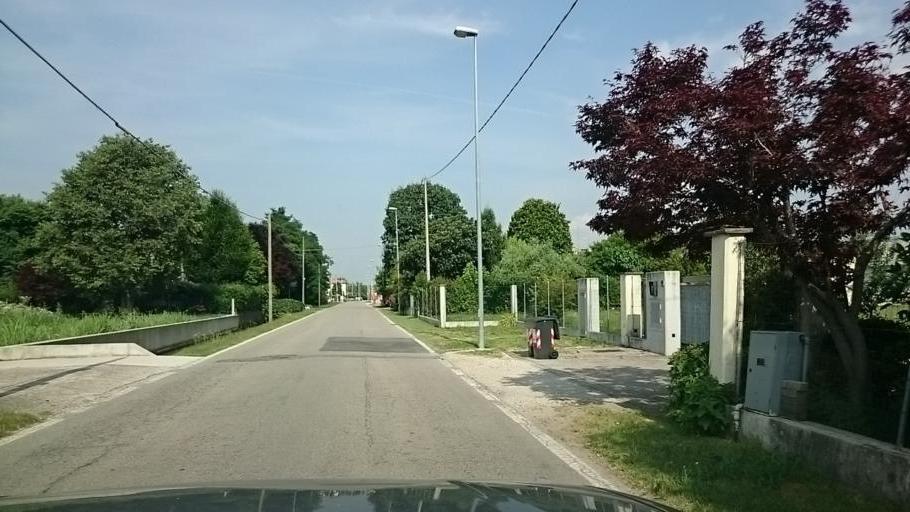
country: IT
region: Veneto
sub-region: Provincia di Vicenza
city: Rossano Veneto
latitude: 45.7120
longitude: 11.8120
